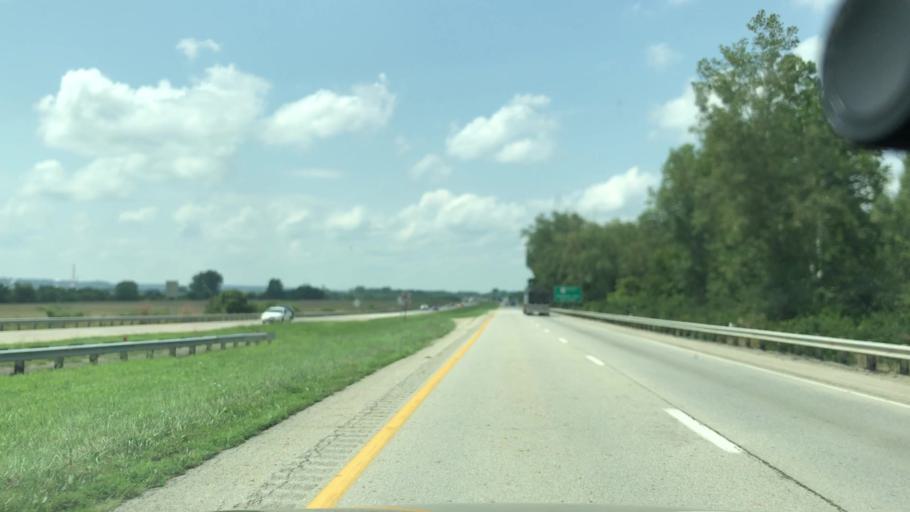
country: US
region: Ohio
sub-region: Ross County
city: Chillicothe
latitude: 39.3085
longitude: -82.9228
